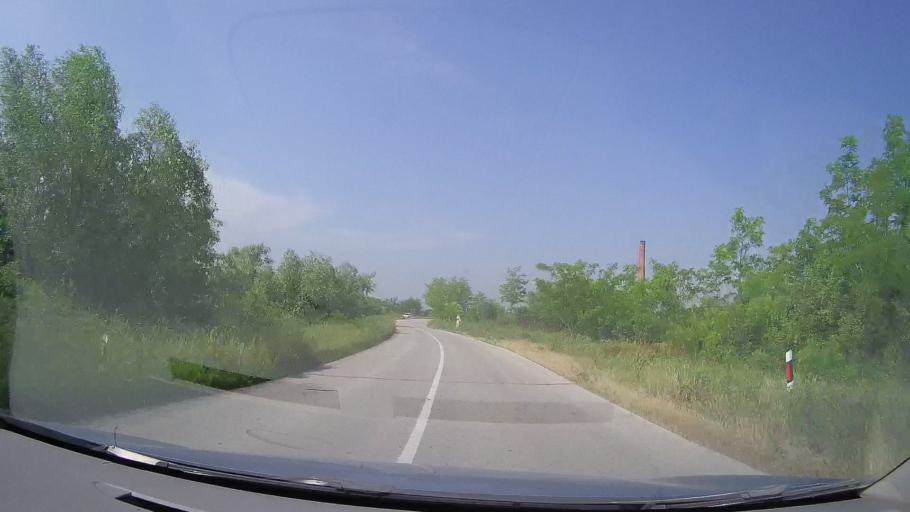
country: RS
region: Autonomna Pokrajina Vojvodina
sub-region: Srednjebanatski Okrug
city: Secanj
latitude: 45.3536
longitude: 20.7657
